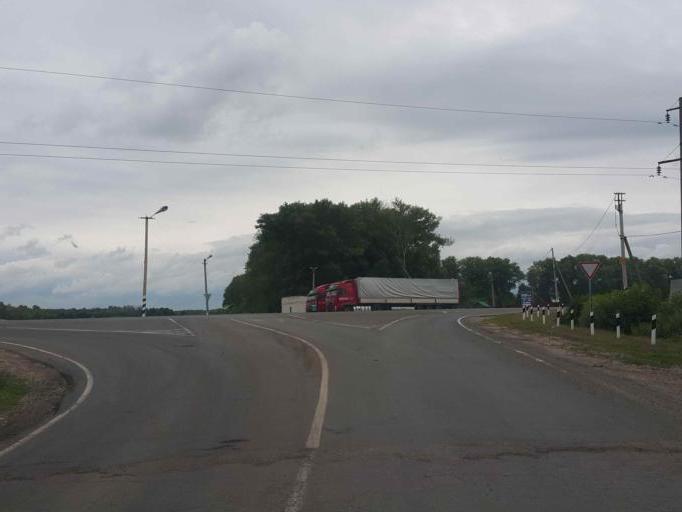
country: RU
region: Tambov
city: Zavoronezhskoye
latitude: 52.9541
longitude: 40.5788
